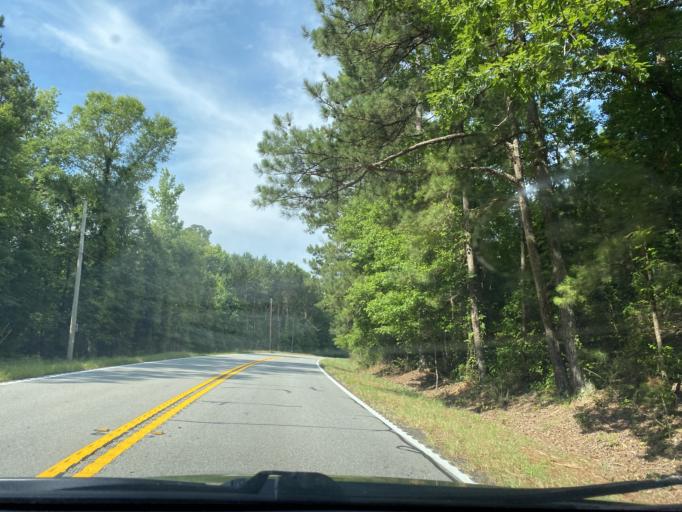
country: US
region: Georgia
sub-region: Coweta County
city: Grantville
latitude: 33.2340
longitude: -84.7394
